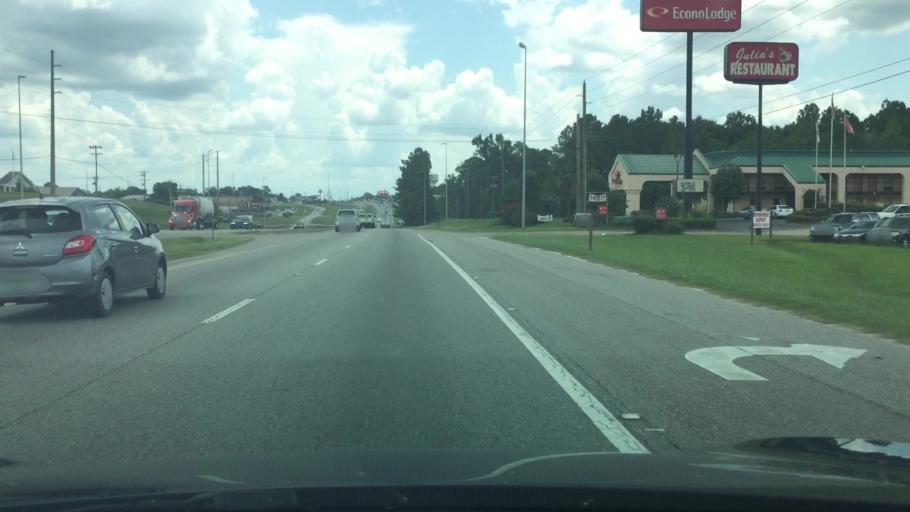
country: US
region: Alabama
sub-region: Pike County
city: Troy
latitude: 31.7898
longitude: -85.9738
